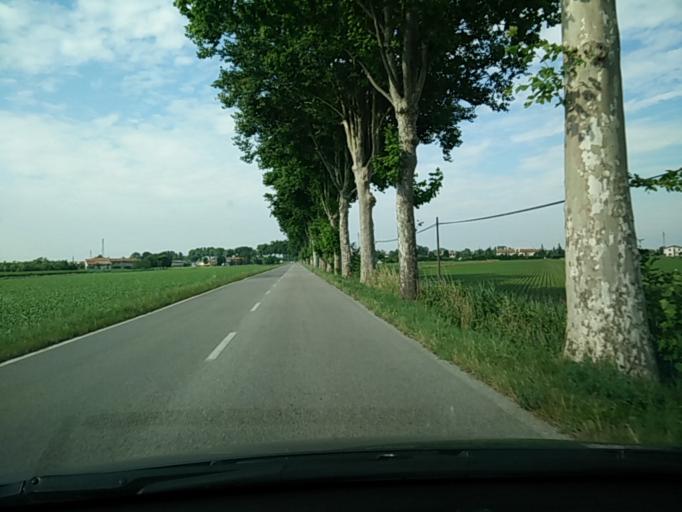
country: IT
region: Veneto
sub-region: Provincia di Venezia
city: Musile di Piave
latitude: 45.5993
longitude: 12.5594
